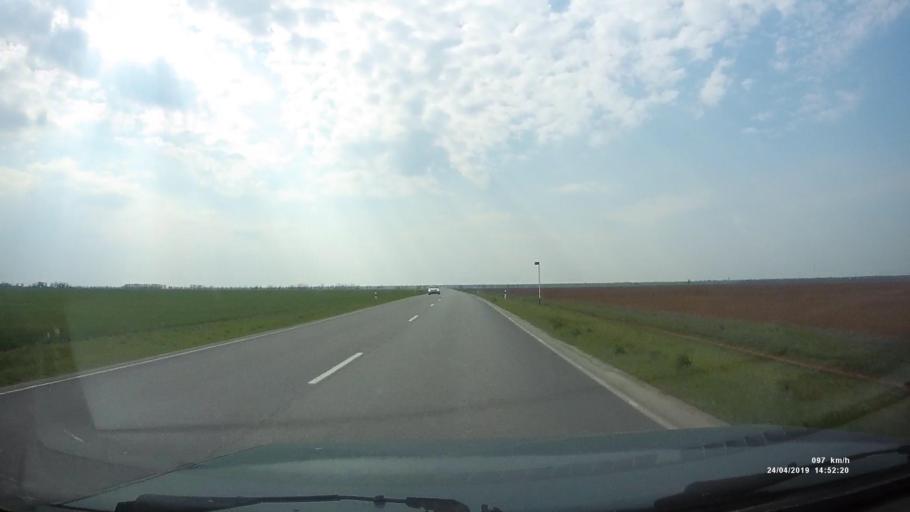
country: RU
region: Rostov
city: Remontnoye
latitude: 46.5301
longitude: 43.6830
